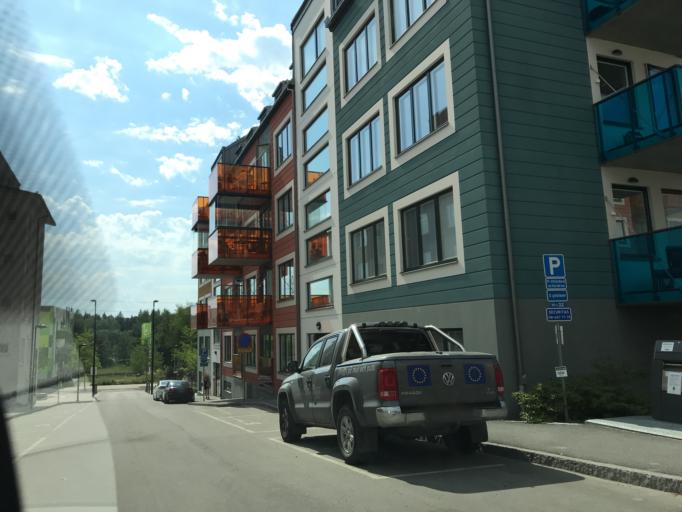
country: SE
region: Stockholm
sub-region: Solna Kommun
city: Rasunda
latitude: 59.3992
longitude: 17.9849
